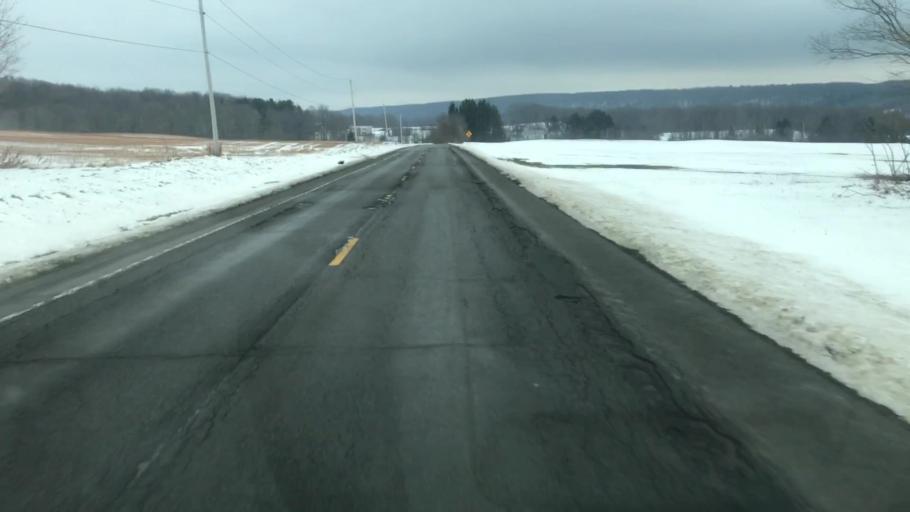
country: US
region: New York
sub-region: Cayuga County
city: Moravia
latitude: 42.7075
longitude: -76.3119
